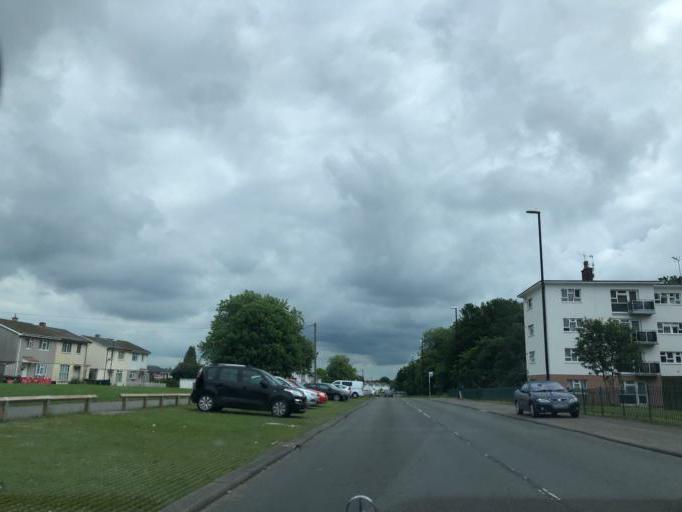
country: GB
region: England
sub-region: Warwickshire
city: Kenilworth
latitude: 52.3932
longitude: -1.5839
